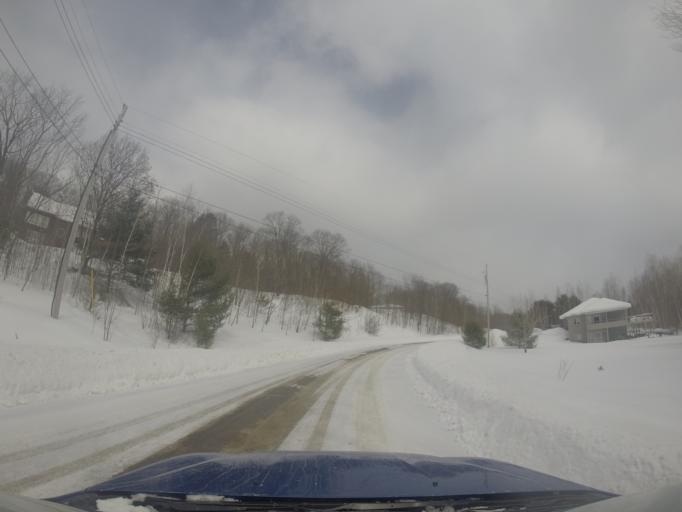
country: CA
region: Ontario
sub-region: Parry Sound District
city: Parry Sound
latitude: 45.3863
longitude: -80.0310
